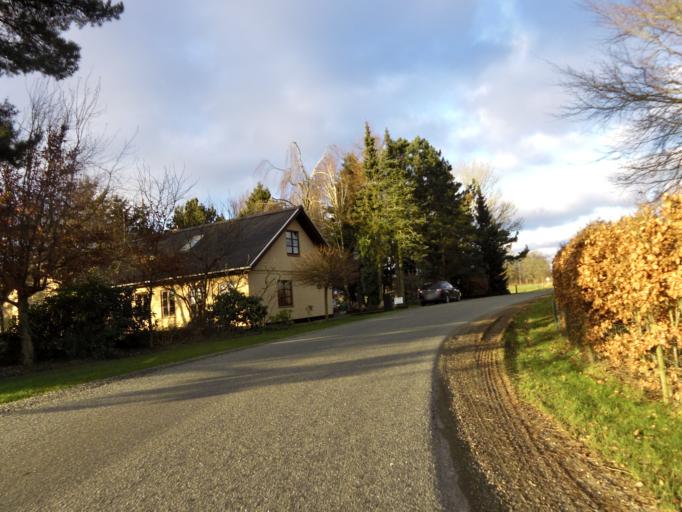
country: DK
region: South Denmark
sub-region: Esbjerg Kommune
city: Ribe
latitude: 55.2908
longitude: 8.8471
